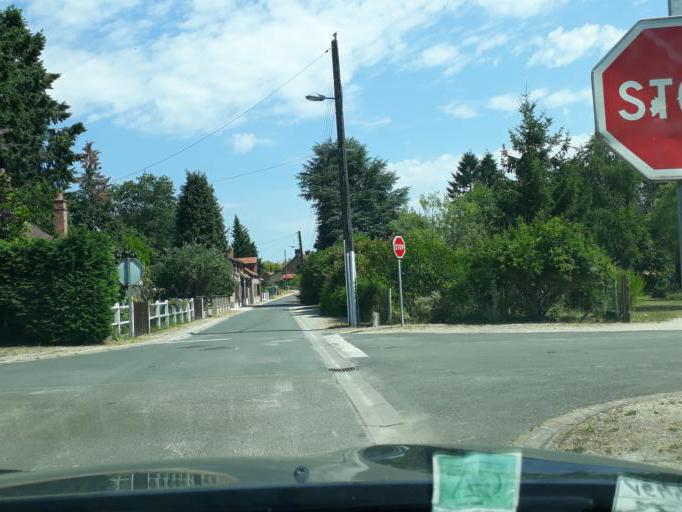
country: FR
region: Centre
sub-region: Departement du Loir-et-Cher
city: Vouzon
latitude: 47.6415
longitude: 2.0541
